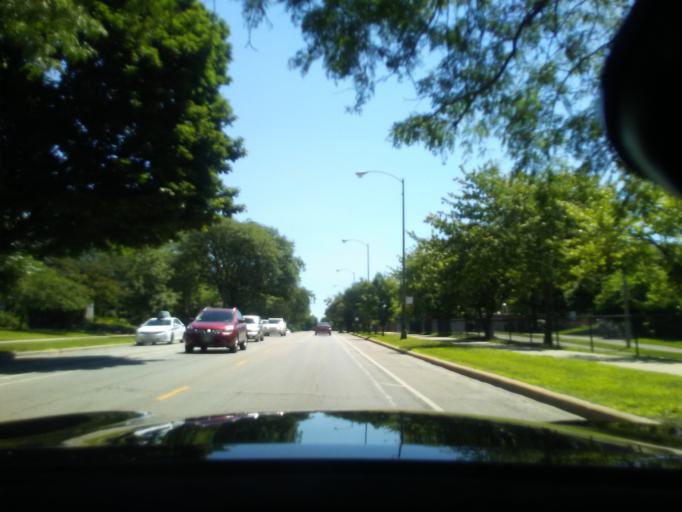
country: US
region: Illinois
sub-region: Cook County
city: Evanston
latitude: 42.0051
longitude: -87.6833
